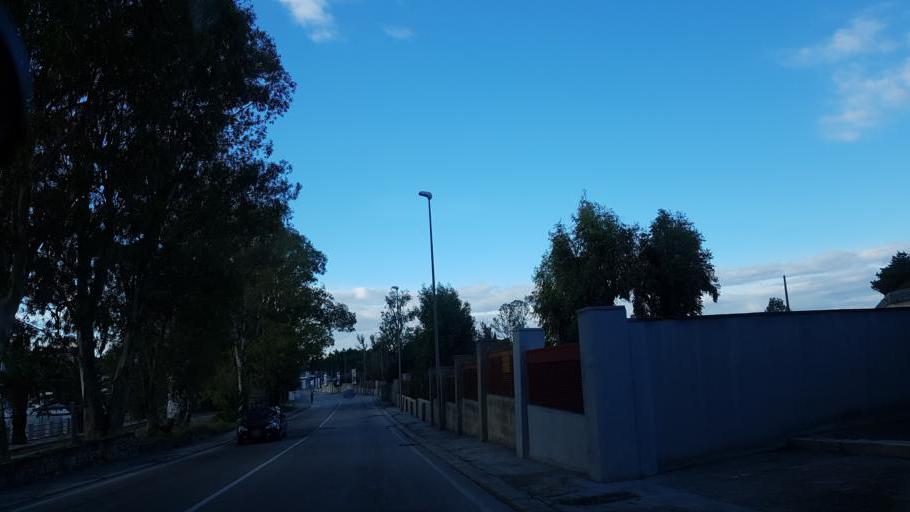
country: IT
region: Apulia
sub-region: Provincia di Brindisi
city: Brindisi
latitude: 40.6427
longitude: 17.9303
